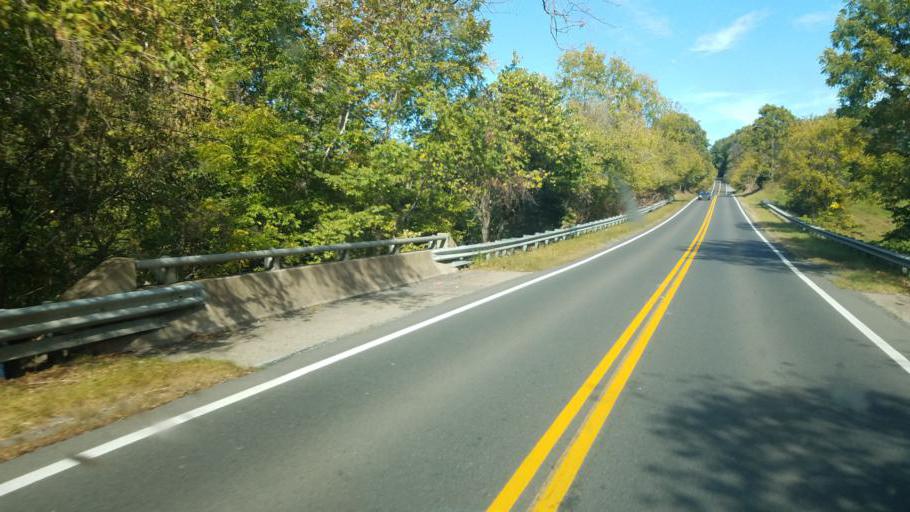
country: US
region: Virginia
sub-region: Warren County
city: Front Royal
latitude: 38.8625
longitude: -78.2599
